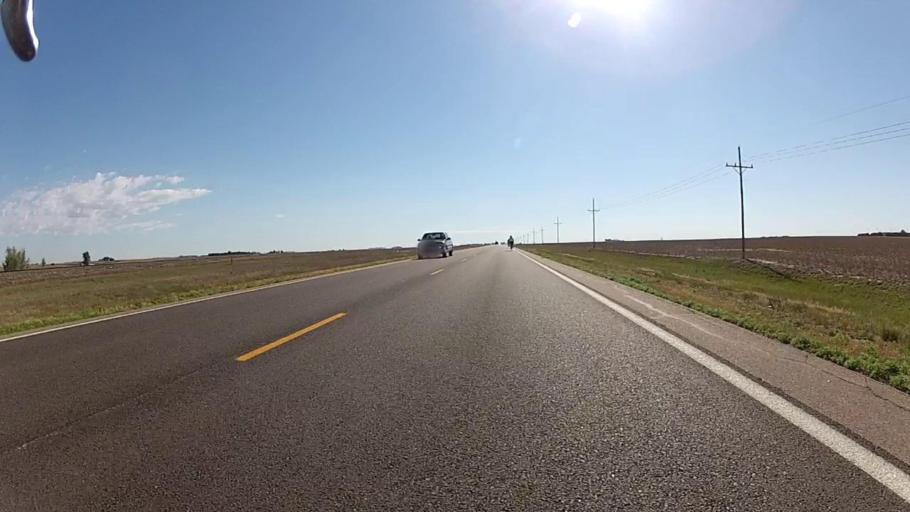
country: US
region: Kansas
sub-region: Gray County
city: Cimarron
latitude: 37.5790
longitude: -100.5152
